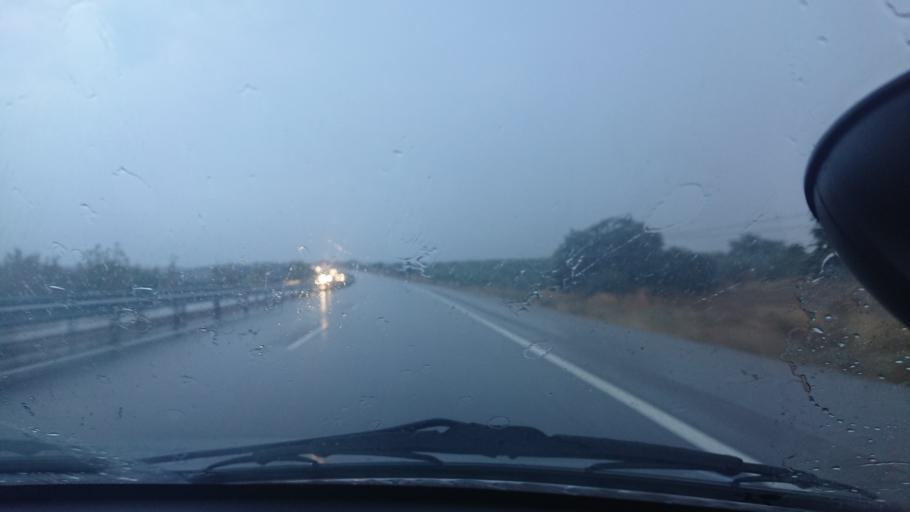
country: TR
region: Manisa
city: Menye
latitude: 38.5301
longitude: 28.3947
